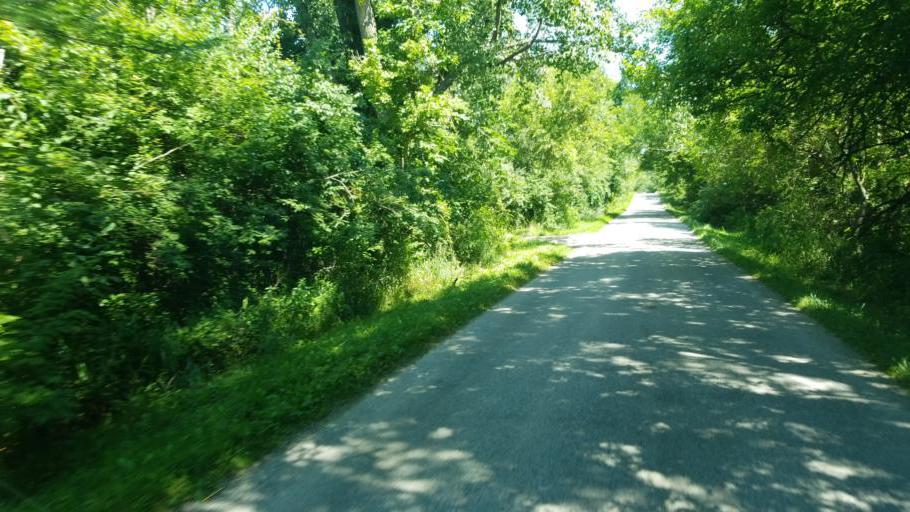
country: US
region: Ohio
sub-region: Delaware County
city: Ashley
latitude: 40.4385
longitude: -83.0498
